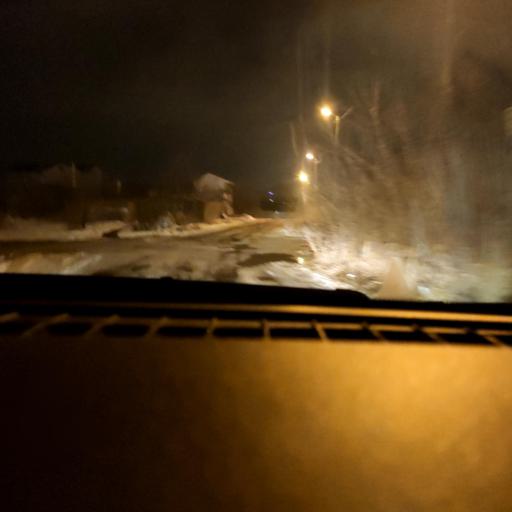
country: RU
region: Voronezj
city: Maslovka
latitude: 51.6112
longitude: 39.2164
